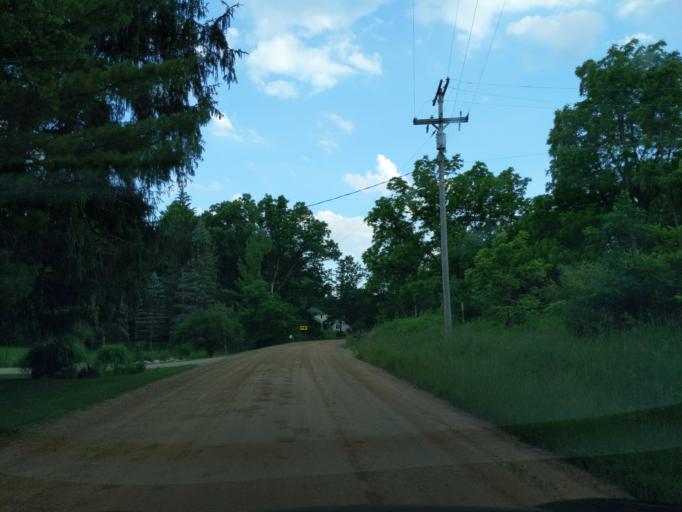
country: US
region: Michigan
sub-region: Shiawassee County
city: Laingsburg
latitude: 42.8253
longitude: -84.3692
